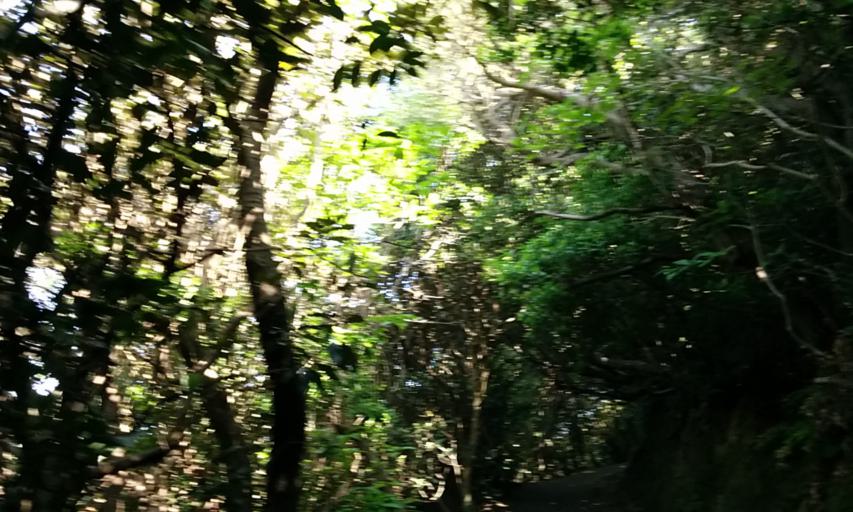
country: JP
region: Oita
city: Tsukumiura
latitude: 33.3461
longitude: 132.0192
